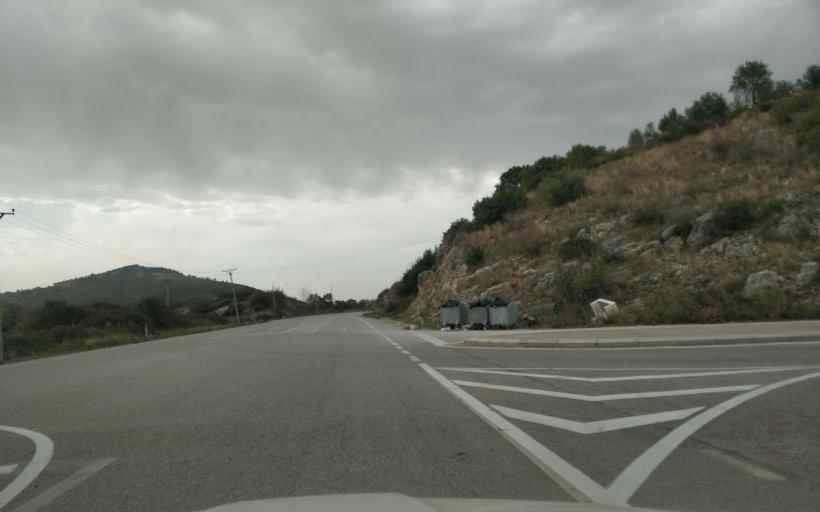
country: AL
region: Fier
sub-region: Rrethi i Mallakastres
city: Kute
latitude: 40.5143
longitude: 19.7458
